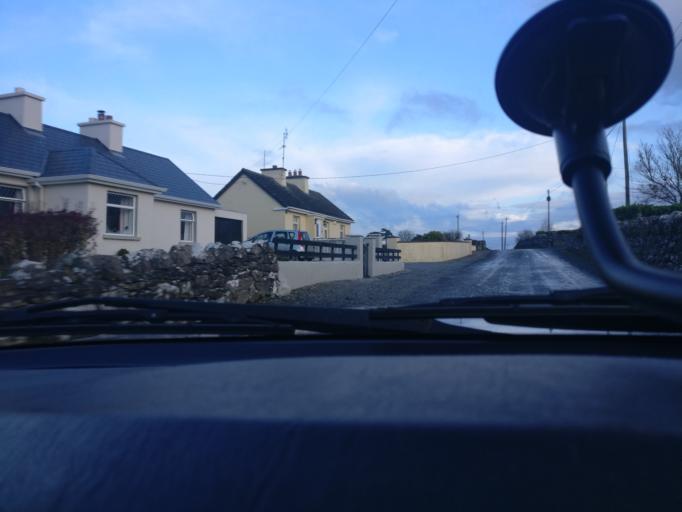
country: IE
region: Connaught
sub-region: County Galway
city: Loughrea
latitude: 53.1988
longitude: -8.6045
